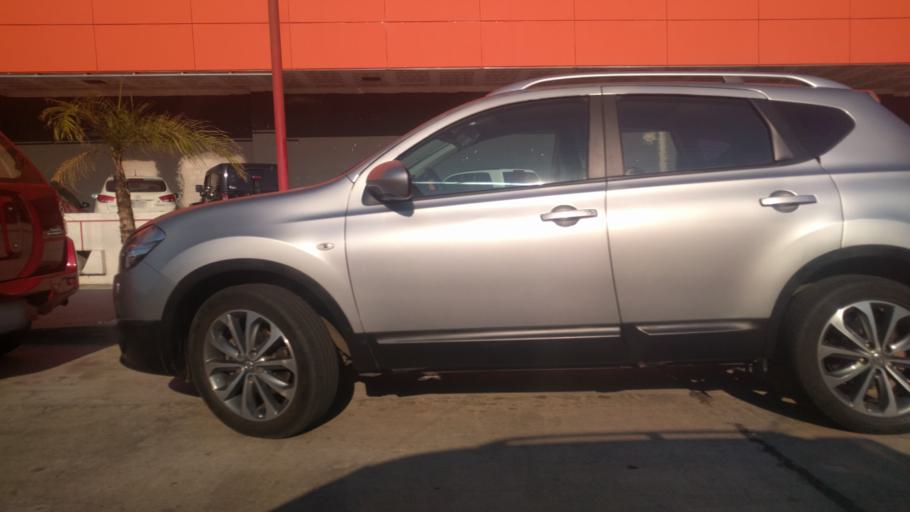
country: BO
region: Santa Cruz
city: Santa Cruz de la Sierra
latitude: -17.7547
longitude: -63.2003
